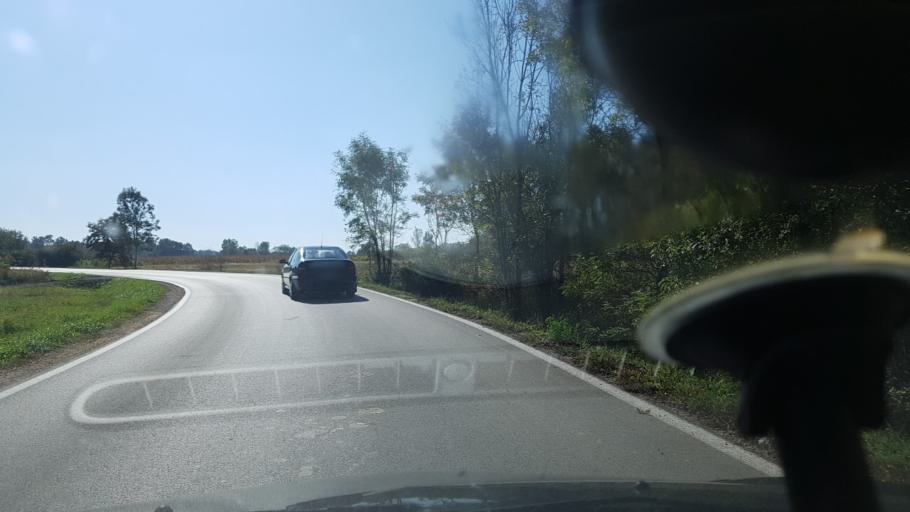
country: HR
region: Zagrebacka
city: Lupoglav
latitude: 45.7276
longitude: 16.3037
